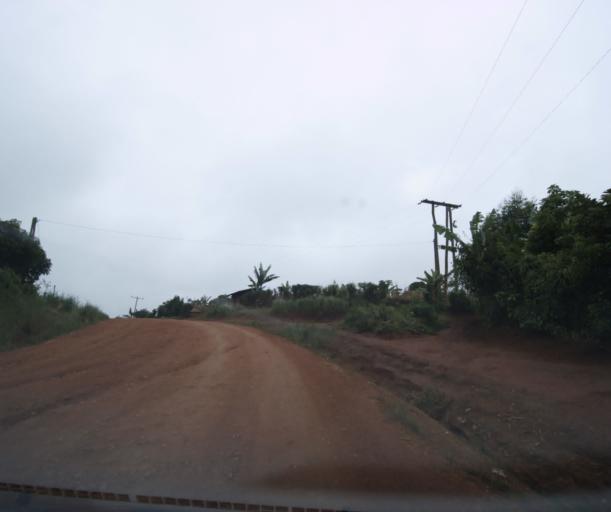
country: CM
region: West
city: Dschang
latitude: 5.5107
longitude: 9.9832
